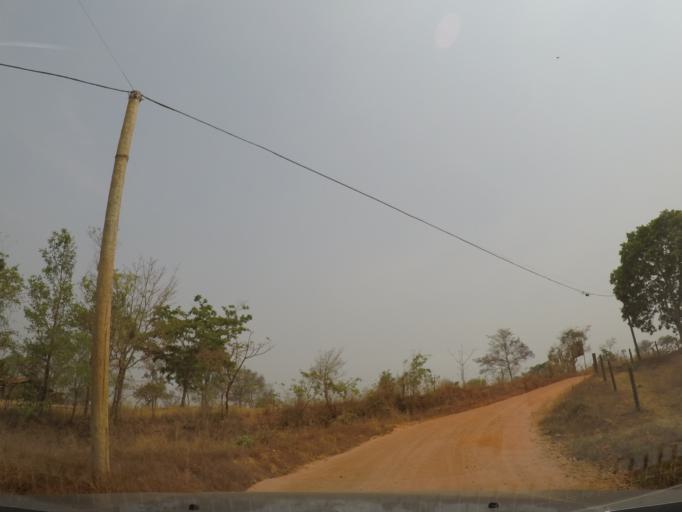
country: BR
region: Goias
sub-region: Pirenopolis
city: Pirenopolis
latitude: -15.8366
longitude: -48.9524
